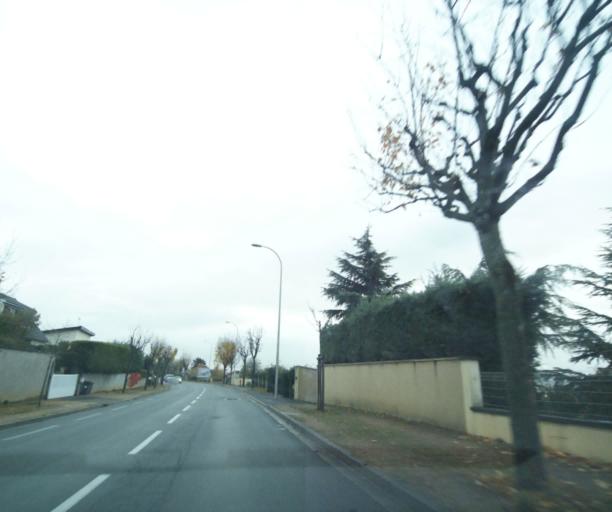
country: FR
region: Auvergne
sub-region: Departement du Puy-de-Dome
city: Cournon-d'Auvergne
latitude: 45.7412
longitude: 3.1837
